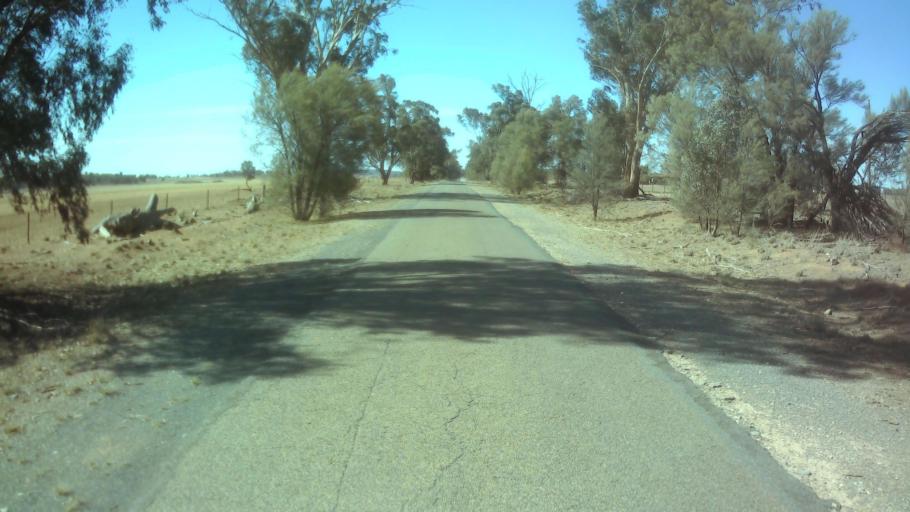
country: AU
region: New South Wales
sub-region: Forbes
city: Forbes
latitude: -33.7267
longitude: 147.7441
